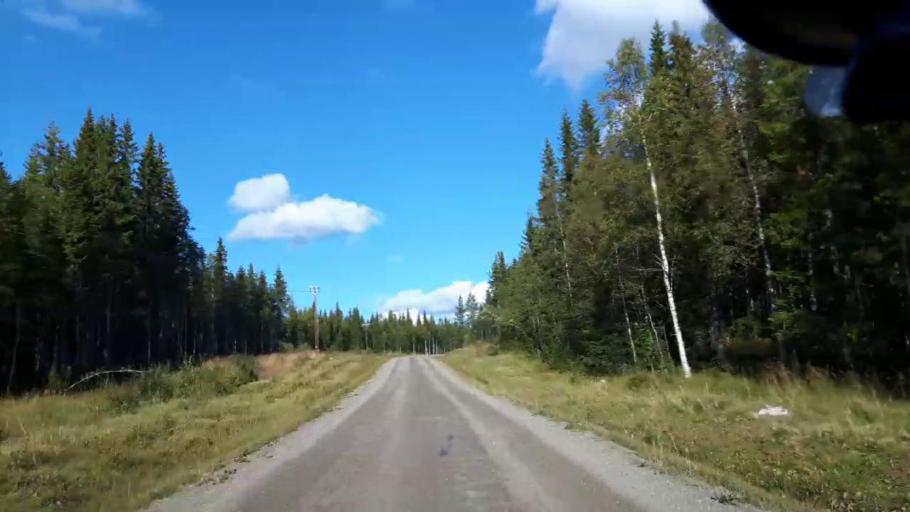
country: SE
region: Jaemtland
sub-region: Ragunda Kommun
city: Hammarstrand
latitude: 63.4422
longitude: 15.9666
